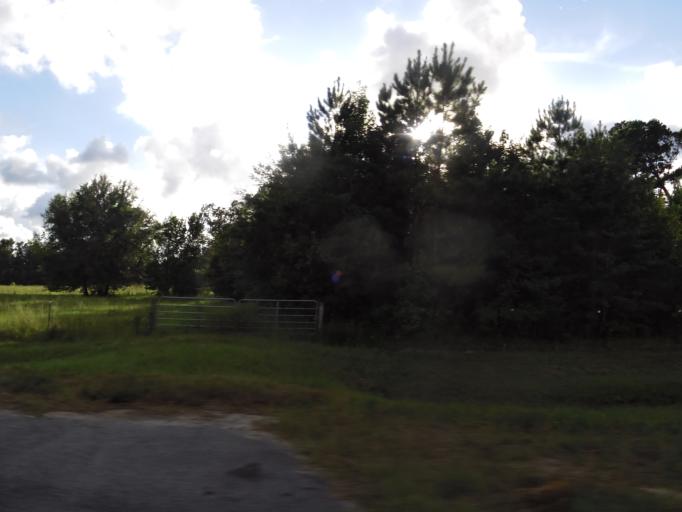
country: US
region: Georgia
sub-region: Liberty County
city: Midway
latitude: 31.7608
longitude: -81.4458
